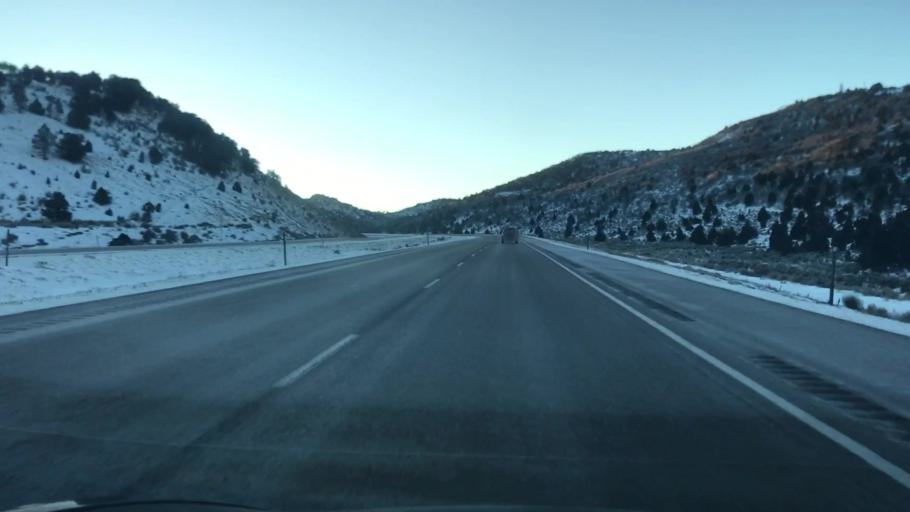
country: US
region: Utah
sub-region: Sevier County
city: Salina
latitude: 38.7910
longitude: -111.5041
